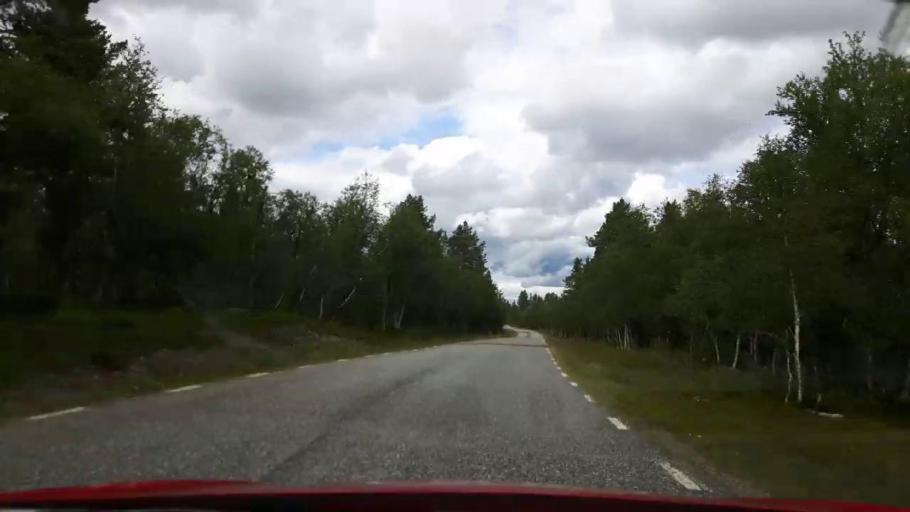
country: NO
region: Hedmark
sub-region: Trysil
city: Innbygda
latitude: 62.1199
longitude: 12.9715
